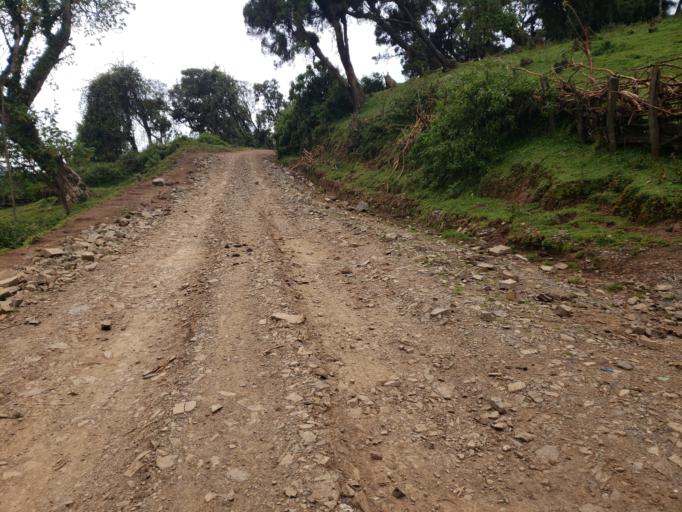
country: ET
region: Oromiya
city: Dodola
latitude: 6.7151
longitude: 39.3743
